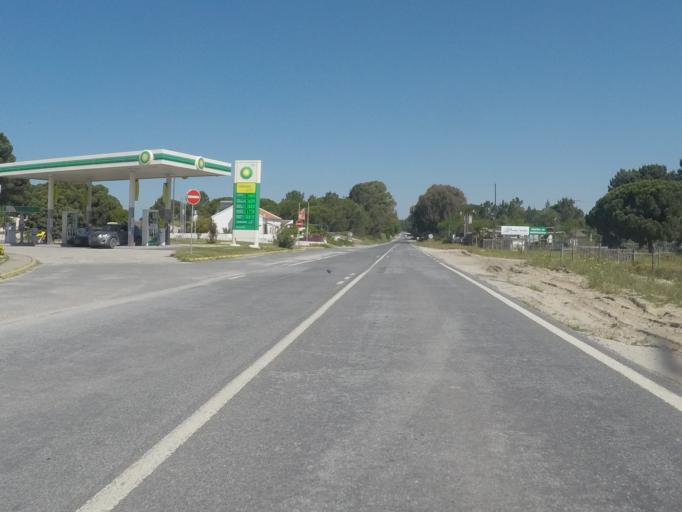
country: PT
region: Setubal
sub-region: Grandola
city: Grandola
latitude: 38.3097
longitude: -8.7425
